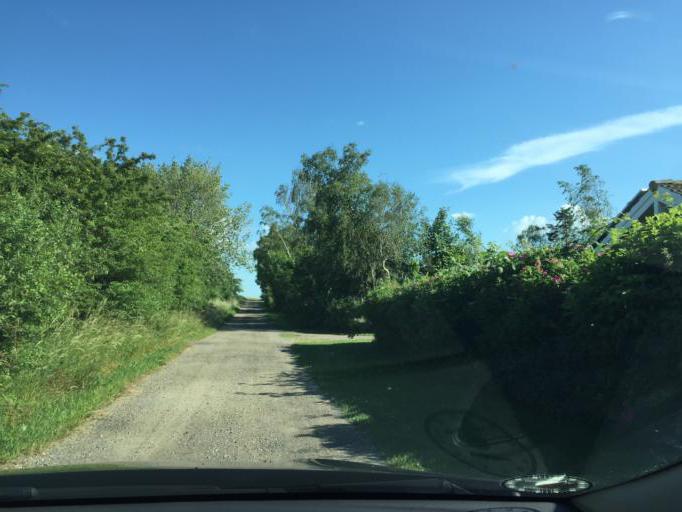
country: DK
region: Zealand
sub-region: Slagelse Kommune
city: Korsor
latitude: 55.2195
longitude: 11.1764
